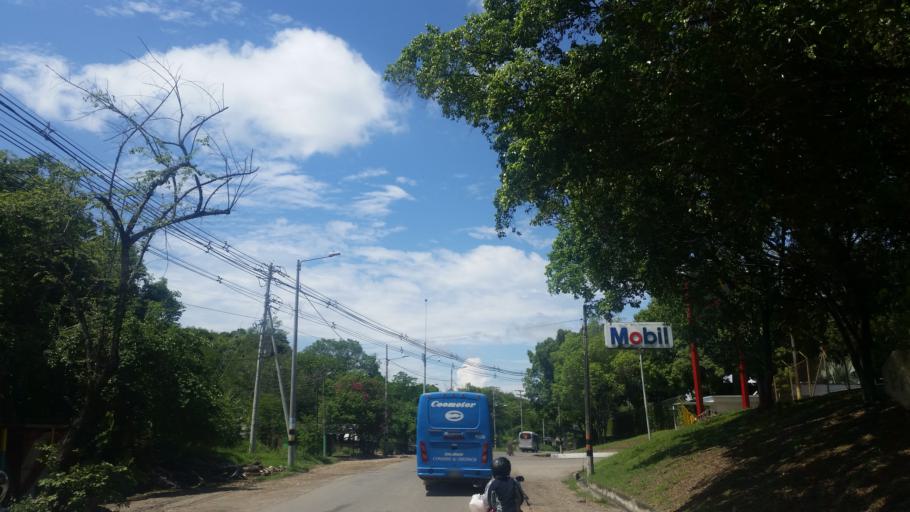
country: CO
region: Huila
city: Neiva
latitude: 2.9863
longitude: -75.2754
